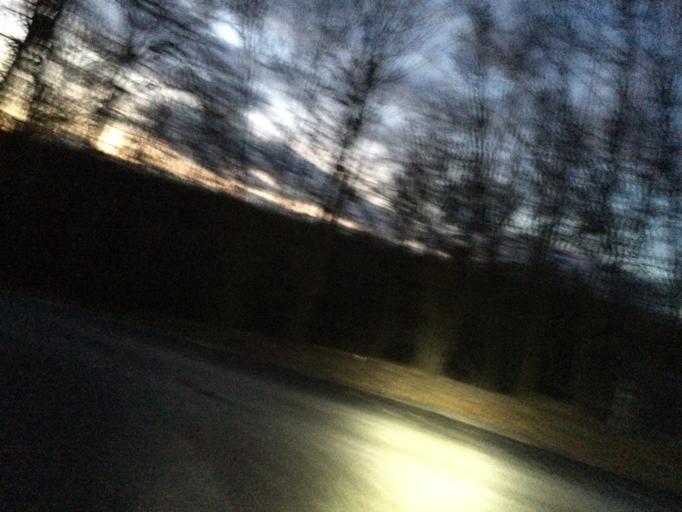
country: FR
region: Picardie
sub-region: Departement de l'Oise
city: Coye-la-Foret
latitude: 49.1547
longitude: 2.4797
